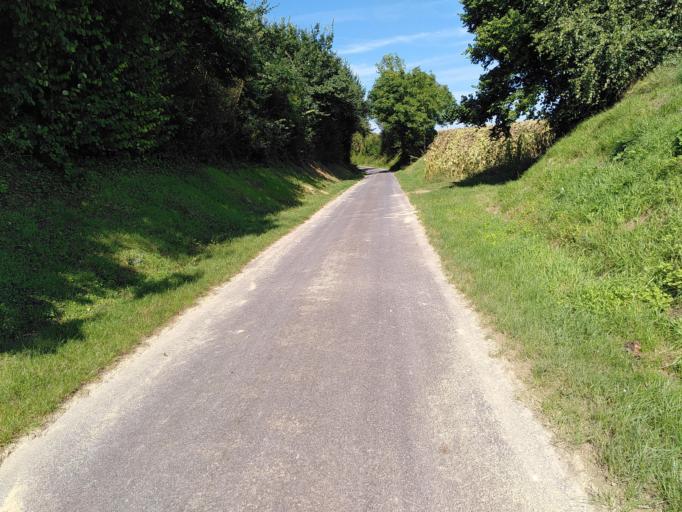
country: FR
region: Champagne-Ardenne
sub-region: Departement des Ardennes
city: Chateau-Porcien
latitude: 49.5129
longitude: 4.1303
